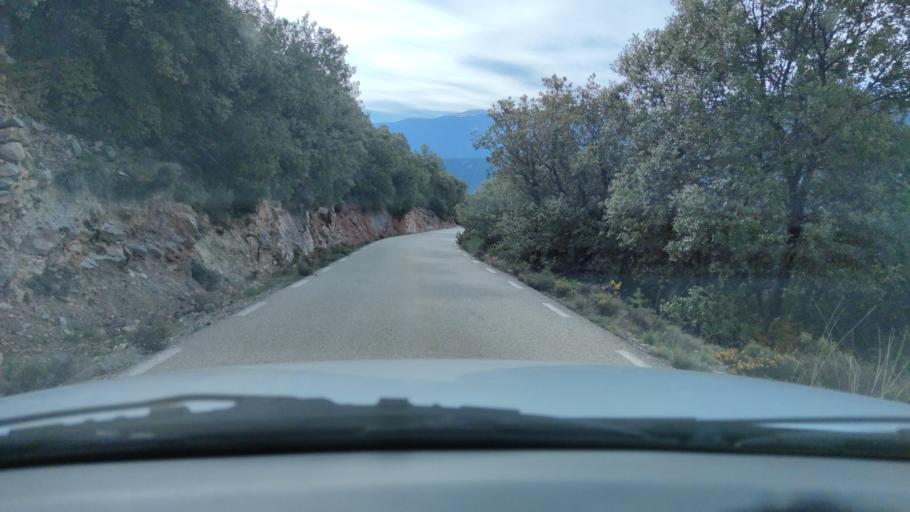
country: ES
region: Catalonia
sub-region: Provincia de Lleida
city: la Seu d'Urgell
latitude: 42.2513
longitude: 1.4115
